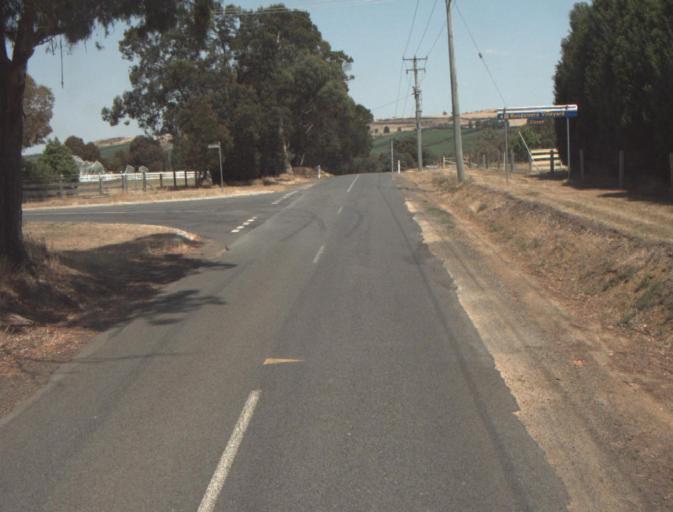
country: AU
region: Tasmania
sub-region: Launceston
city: Newstead
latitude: -41.5000
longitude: 147.2064
